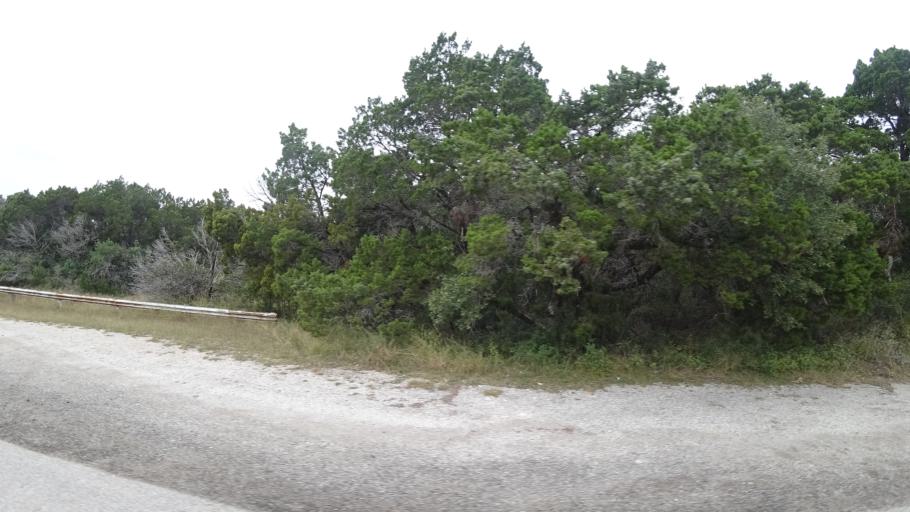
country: US
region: Texas
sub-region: Travis County
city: Hudson Bend
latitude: 30.3955
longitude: -97.9105
